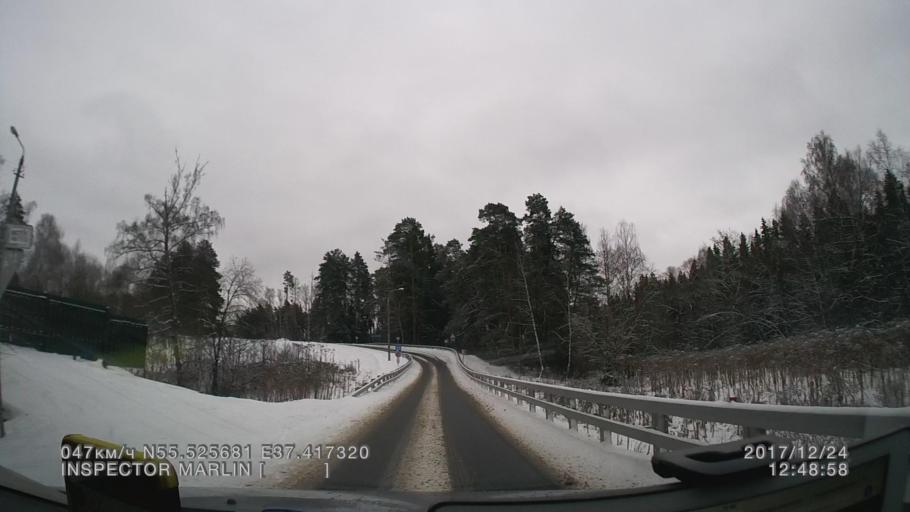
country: RU
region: Moskovskaya
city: Filimonki
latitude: 55.5256
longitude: 37.4174
